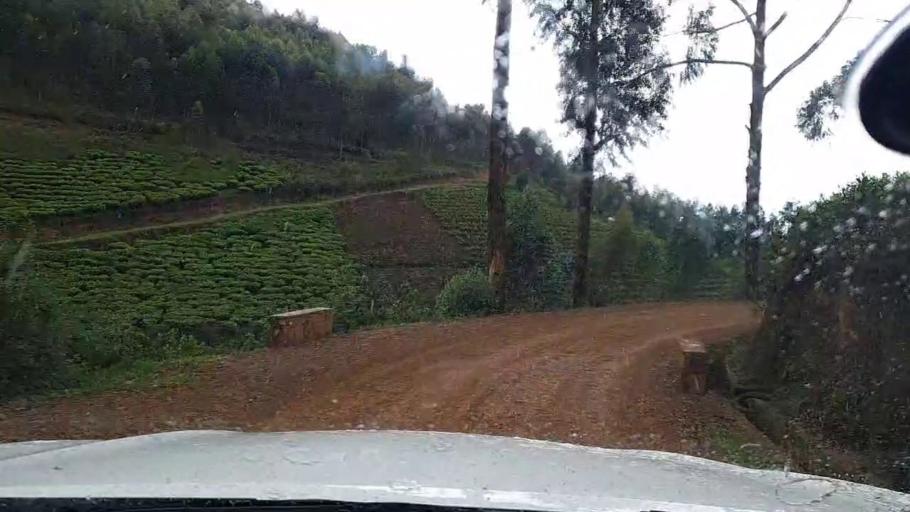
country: RW
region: Western Province
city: Kibuye
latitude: -2.1560
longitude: 29.4304
